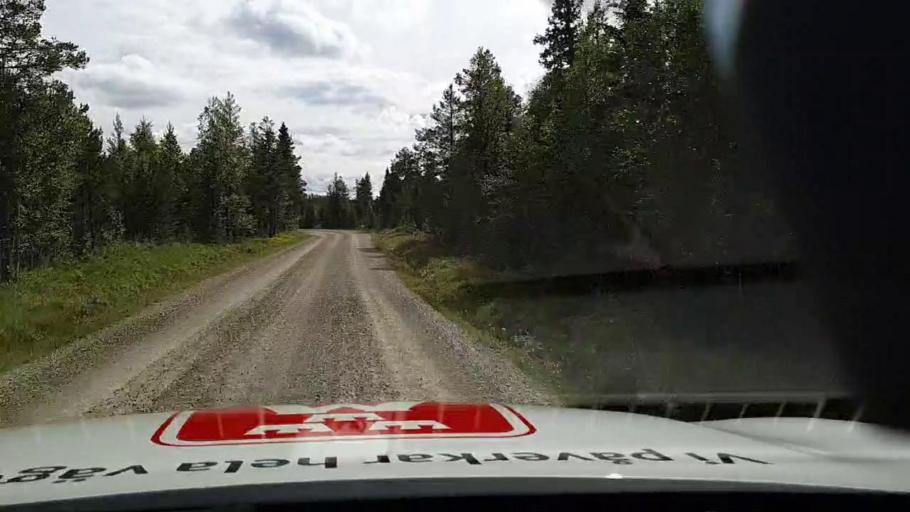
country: SE
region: Jaemtland
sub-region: Are Kommun
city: Jarpen
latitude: 62.5419
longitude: 13.4732
